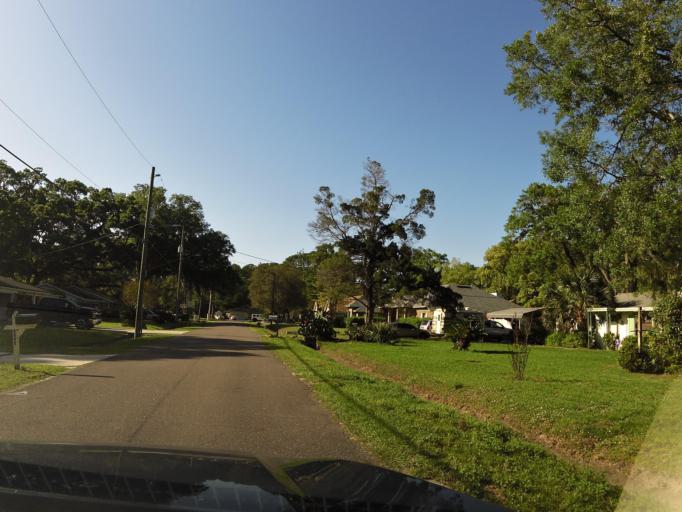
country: US
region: Florida
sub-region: Duval County
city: Jacksonville
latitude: 30.2790
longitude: -81.5840
